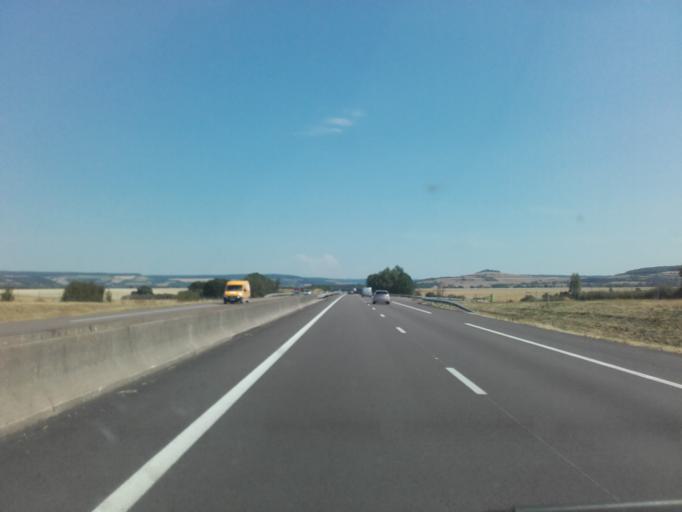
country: FR
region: Bourgogne
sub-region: Departement de la Cote-d'Or
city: Vitteaux
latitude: 47.3641
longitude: 4.4168
